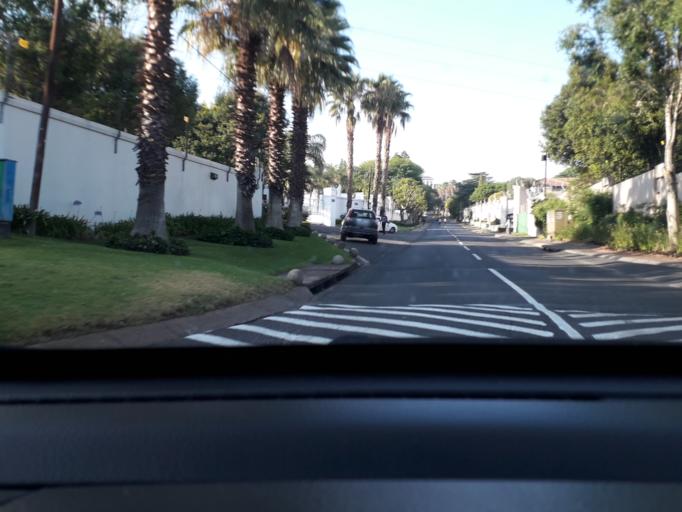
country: ZA
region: Gauteng
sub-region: City of Johannesburg Metropolitan Municipality
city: Modderfontein
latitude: -26.0853
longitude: 28.0566
